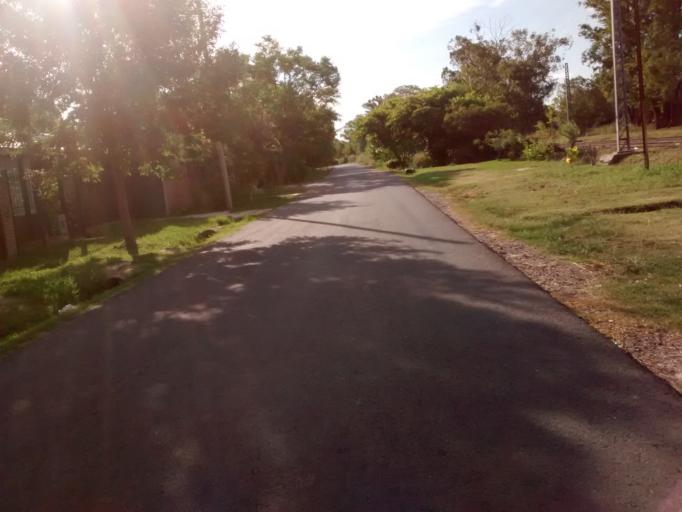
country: AR
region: Buenos Aires
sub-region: Partido de La Plata
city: La Plata
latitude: -34.8467
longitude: -58.0827
